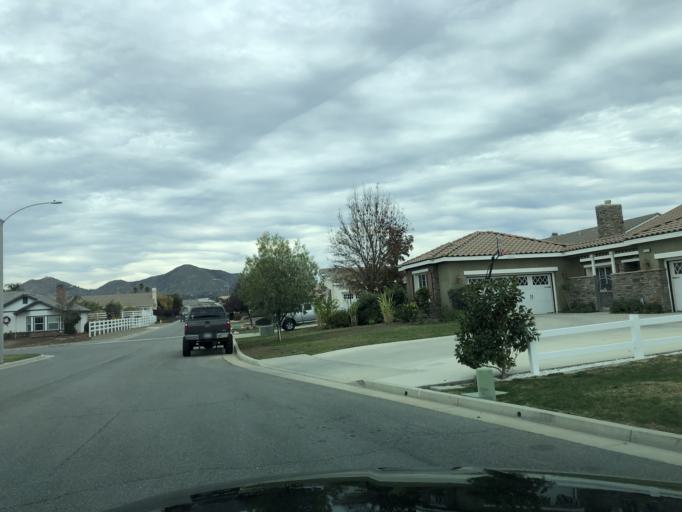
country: US
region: California
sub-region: Riverside County
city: Wildomar
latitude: 33.6118
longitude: -117.2781
